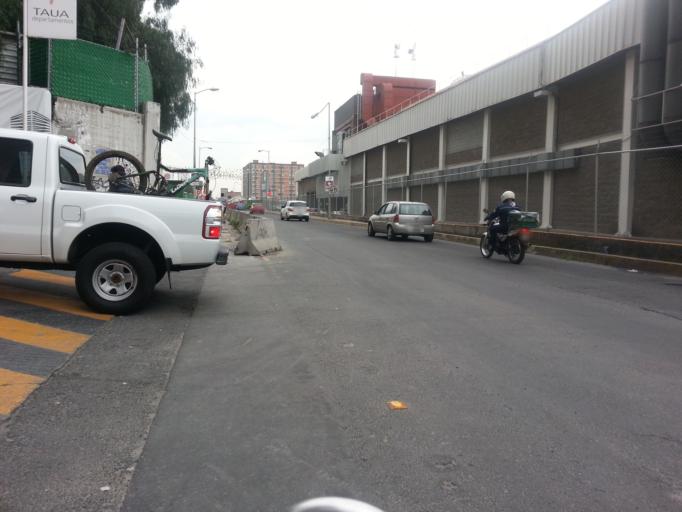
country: MX
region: Mexico City
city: Colonia del Valle
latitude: 19.3859
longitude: -99.1916
